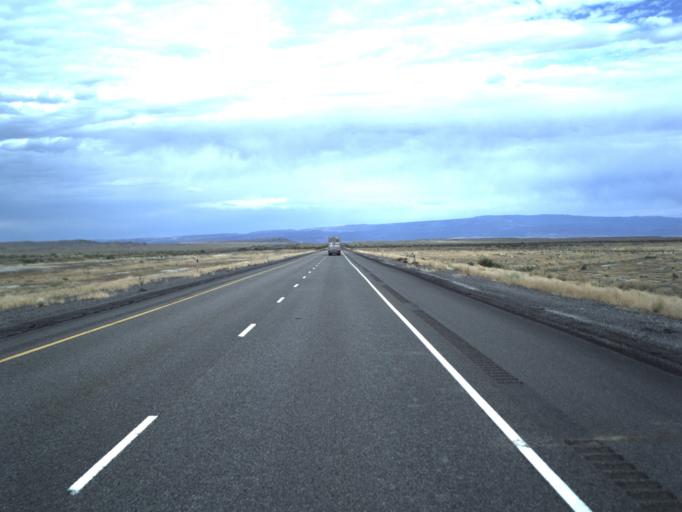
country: US
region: Utah
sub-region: Grand County
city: Moab
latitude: 38.9418
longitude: -109.5761
